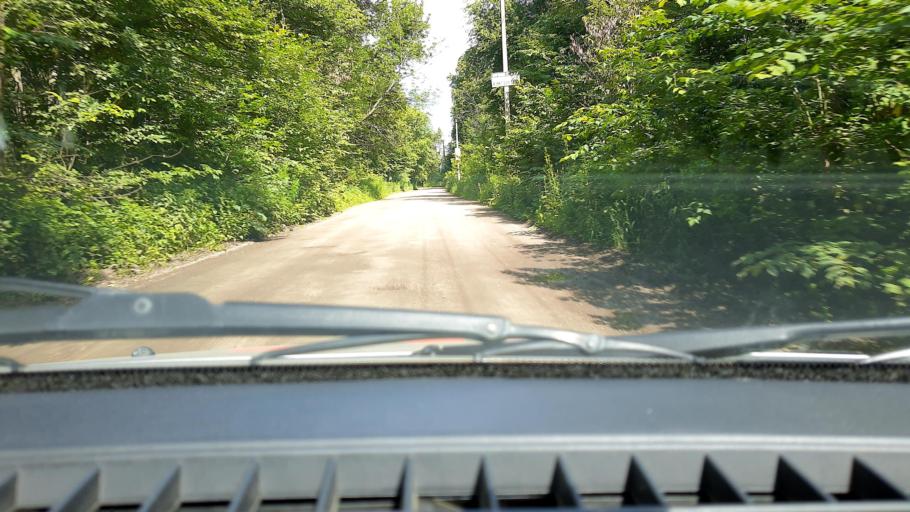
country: RU
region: Bashkortostan
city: Ufa
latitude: 54.6896
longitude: 56.0534
